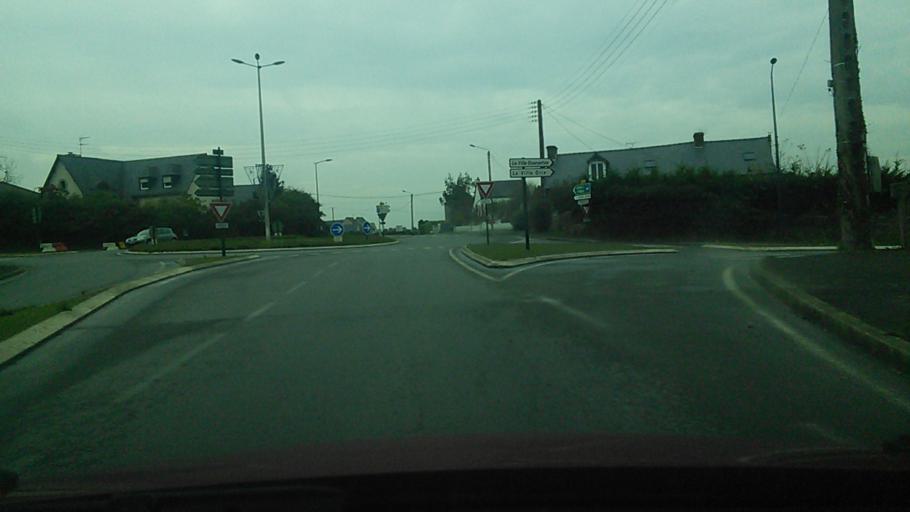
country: FR
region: Brittany
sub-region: Departement des Cotes-d'Armor
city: Pommeret
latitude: 48.4702
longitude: -2.6503
